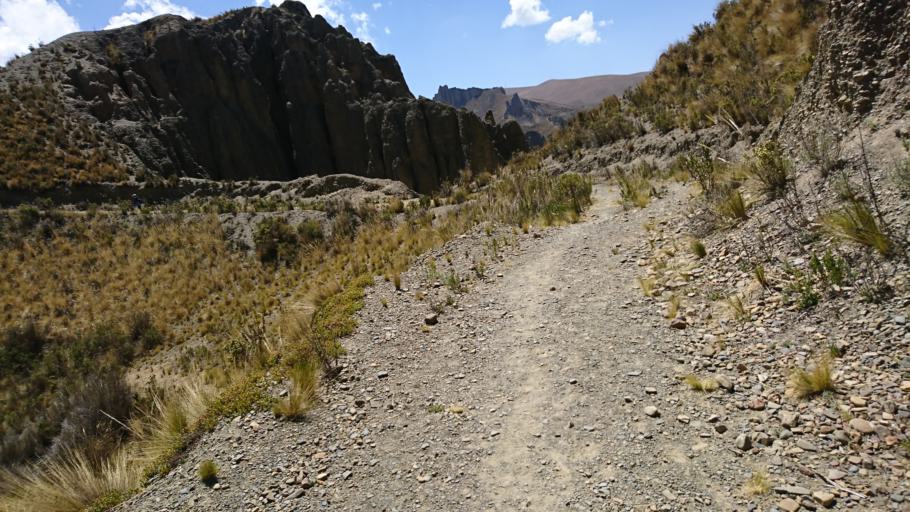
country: BO
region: La Paz
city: La Paz
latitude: -16.5436
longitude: -68.0107
